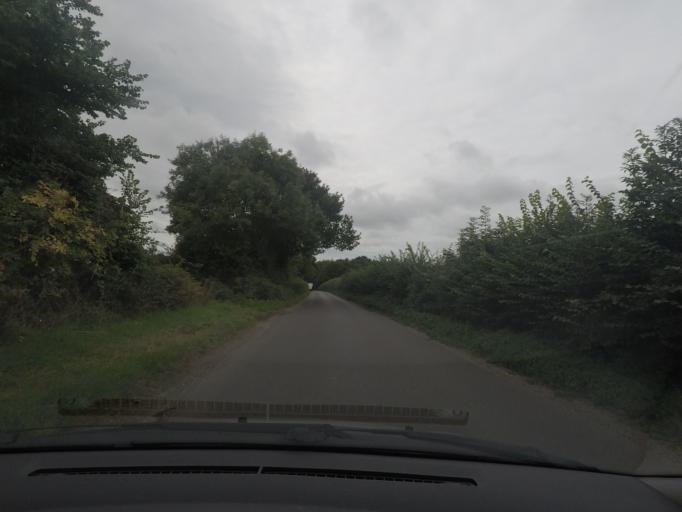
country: GB
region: England
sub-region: Wiltshire
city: Huish
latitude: 51.3541
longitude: -1.7820
